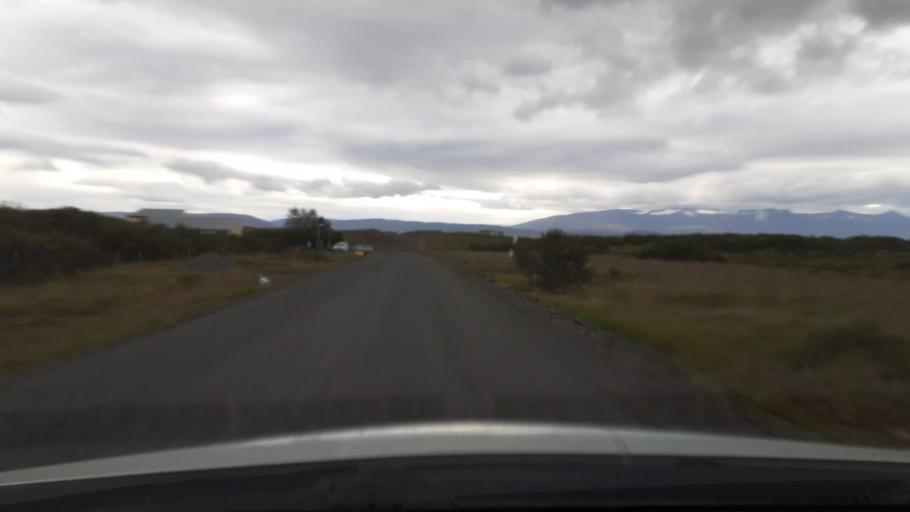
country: IS
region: West
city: Borgarnes
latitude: 64.6752
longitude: -21.7072
